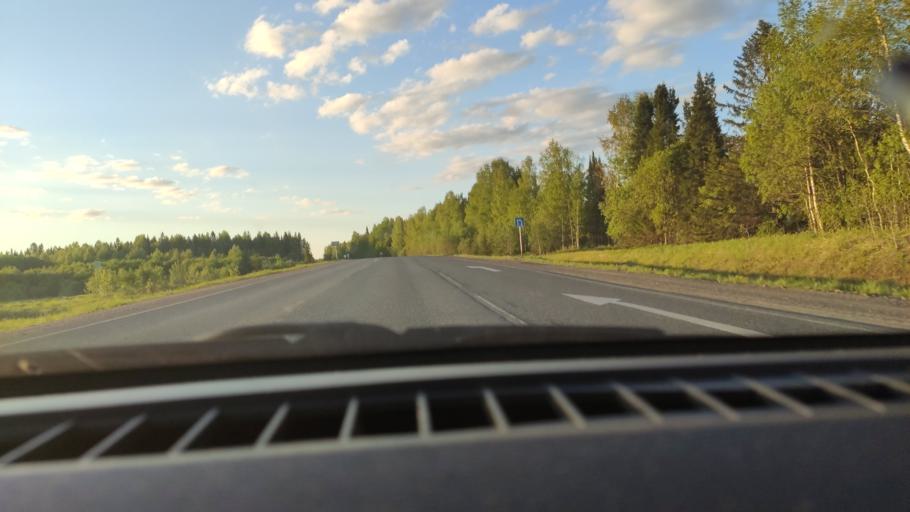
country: RU
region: Perm
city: Dobryanka
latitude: 58.5779
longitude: 56.6512
